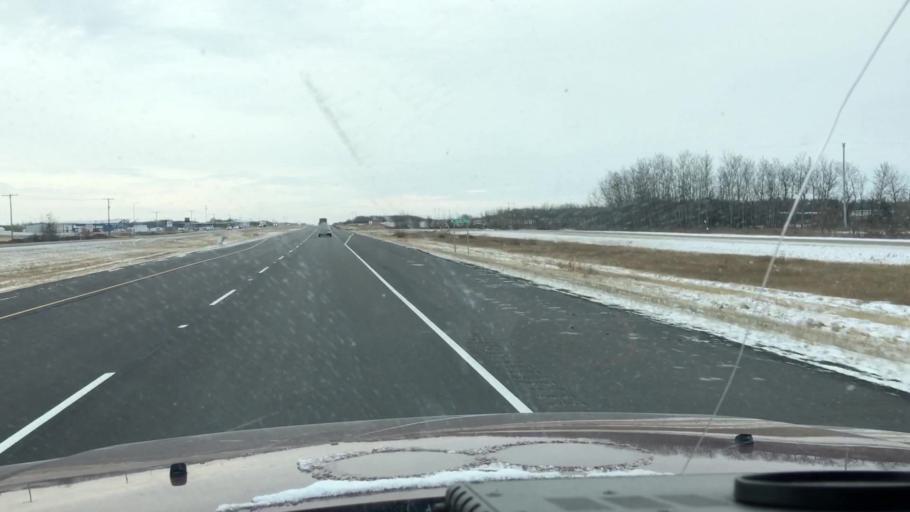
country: CA
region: Saskatchewan
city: Saskatoon
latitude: 51.9714
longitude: -106.5547
